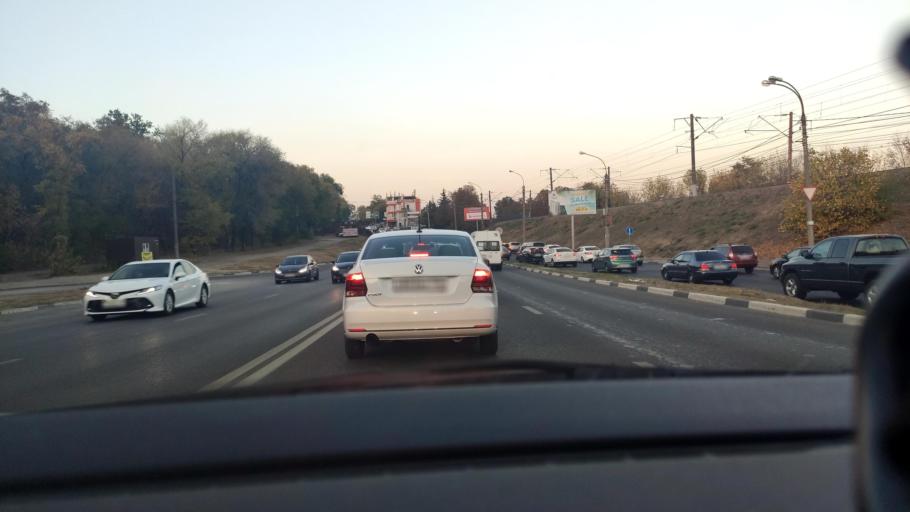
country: RU
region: Voronezj
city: Voronezh
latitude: 51.6966
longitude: 39.2296
